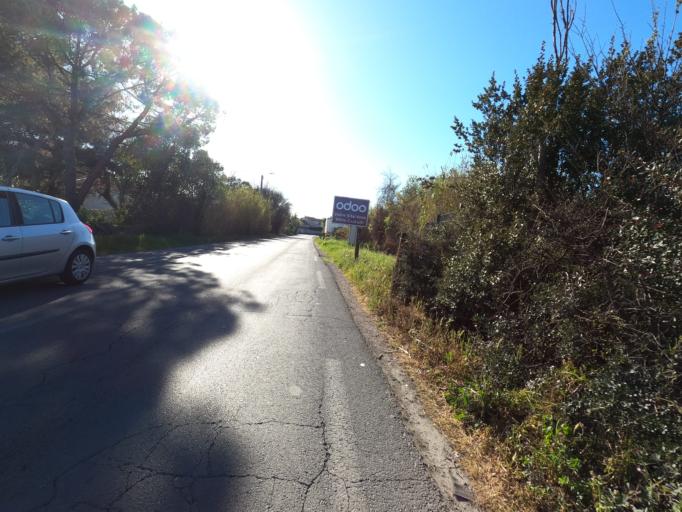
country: FR
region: Languedoc-Roussillon
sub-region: Departement de l'Herault
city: Montpellier
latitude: 43.5859
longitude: 3.8758
